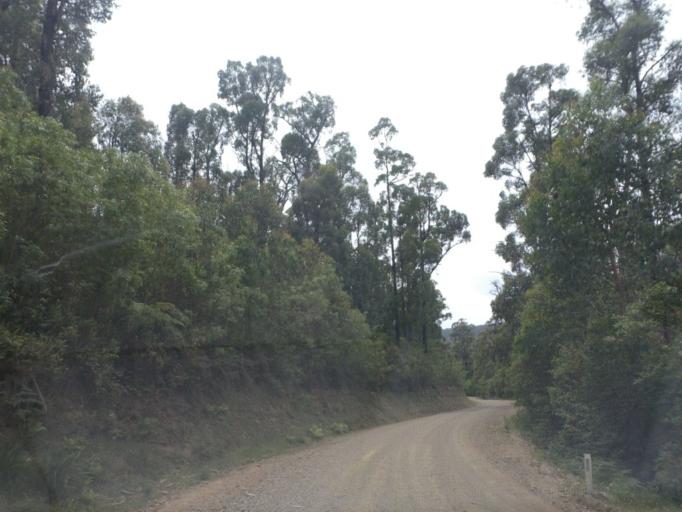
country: AU
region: Victoria
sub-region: Yarra Ranges
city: Healesville
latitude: -37.4519
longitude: 145.5739
